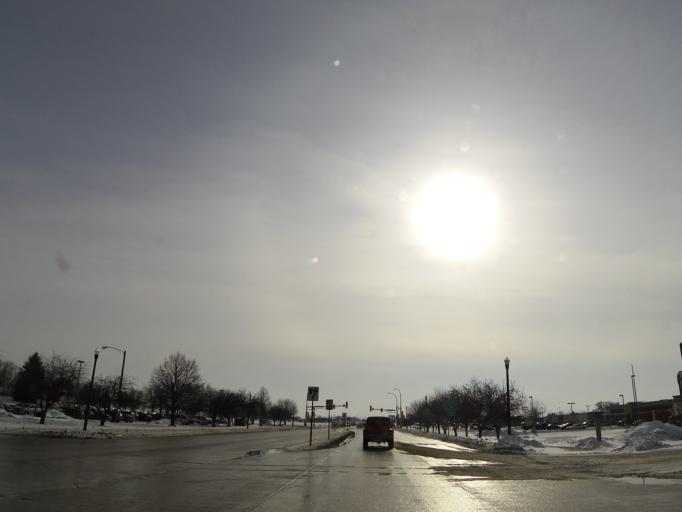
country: US
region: Minnesota
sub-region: McLeod County
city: Hutchinson
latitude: 44.8766
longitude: -94.3757
